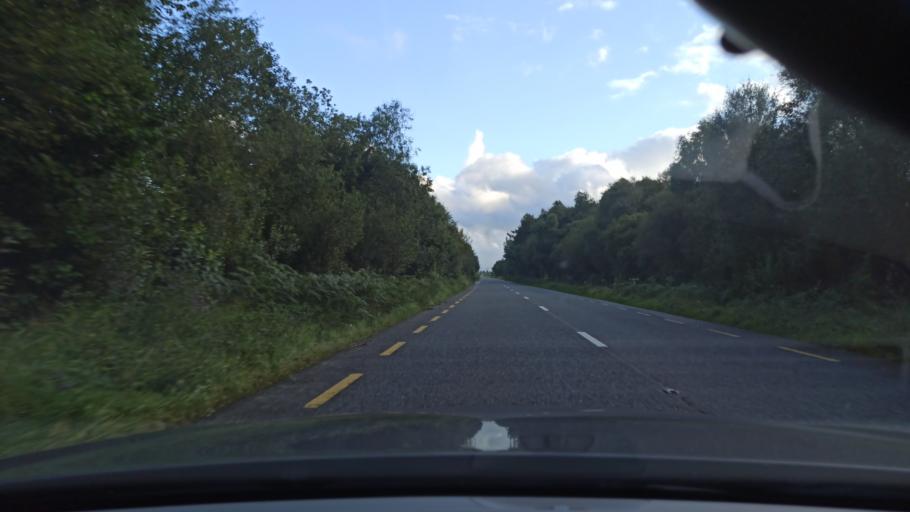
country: IE
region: Munster
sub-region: North Tipperary
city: Templemore
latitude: 52.8693
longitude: -7.8113
